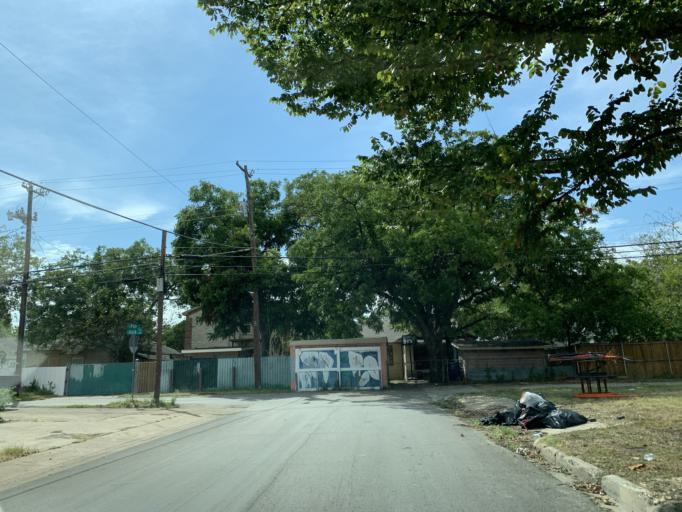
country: US
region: Texas
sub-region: Dallas County
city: Cockrell Hill
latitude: 32.7403
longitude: -96.8396
